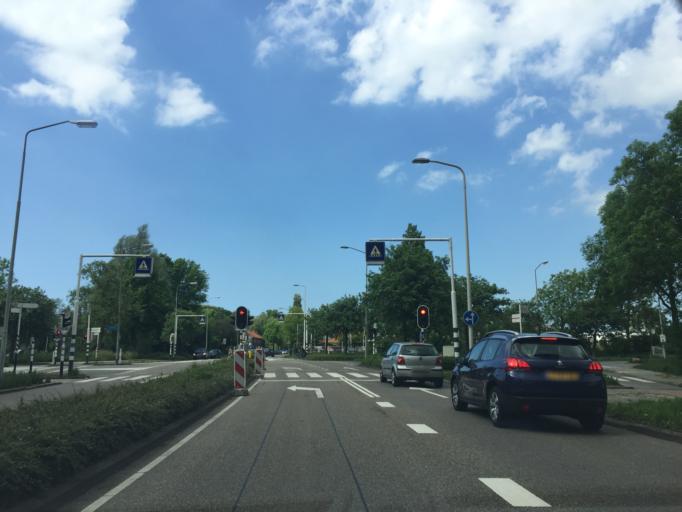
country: NL
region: South Holland
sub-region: Gemeente Voorschoten
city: Voorschoten
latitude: 52.1457
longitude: 4.4642
